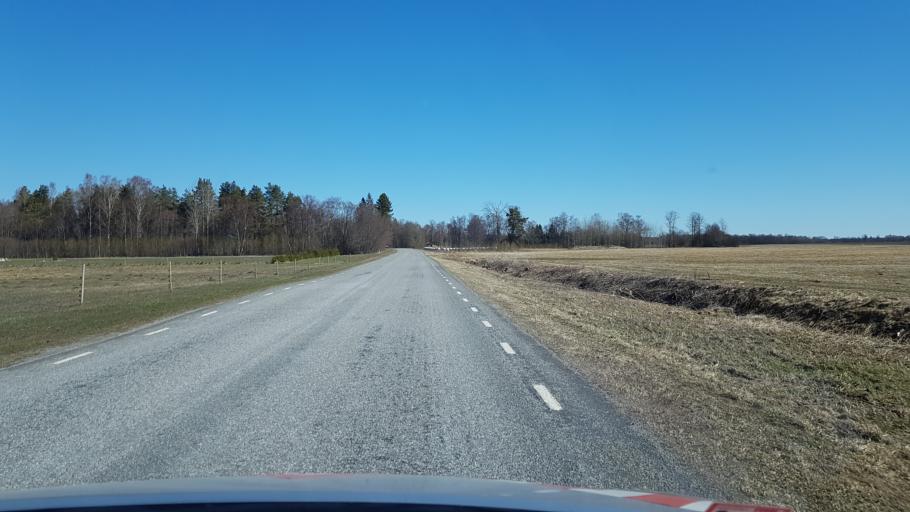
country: EE
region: Laeaene-Virumaa
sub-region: Haljala vald
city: Haljala
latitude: 59.4619
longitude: 26.2366
